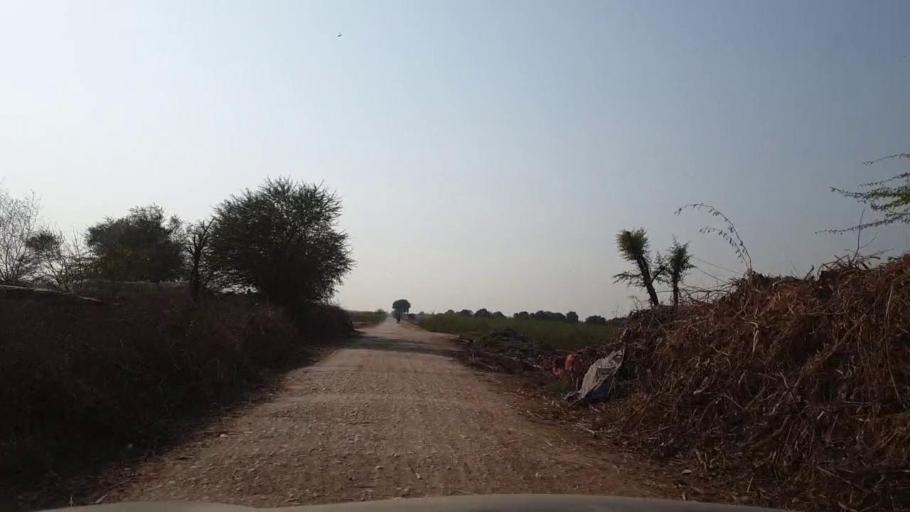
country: PK
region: Sindh
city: Tando Allahyar
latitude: 25.5817
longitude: 68.7910
